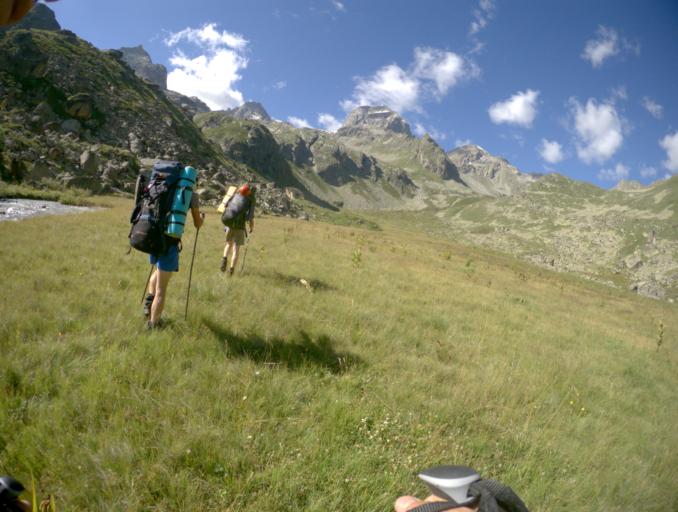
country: RU
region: Karachayevo-Cherkesiya
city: Uchkulan
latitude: 43.3311
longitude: 42.1151
